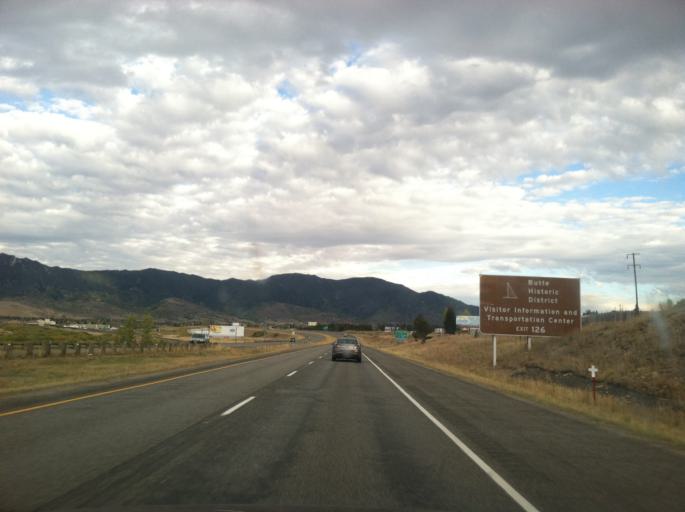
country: US
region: Montana
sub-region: Silver Bow County
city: Butte
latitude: 45.9944
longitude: -112.5605
